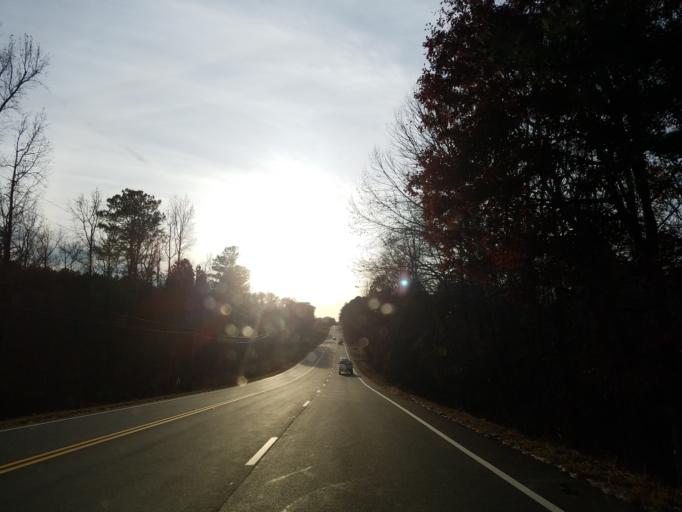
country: US
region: Georgia
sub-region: Carroll County
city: Temple
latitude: 33.7318
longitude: -85.0632
